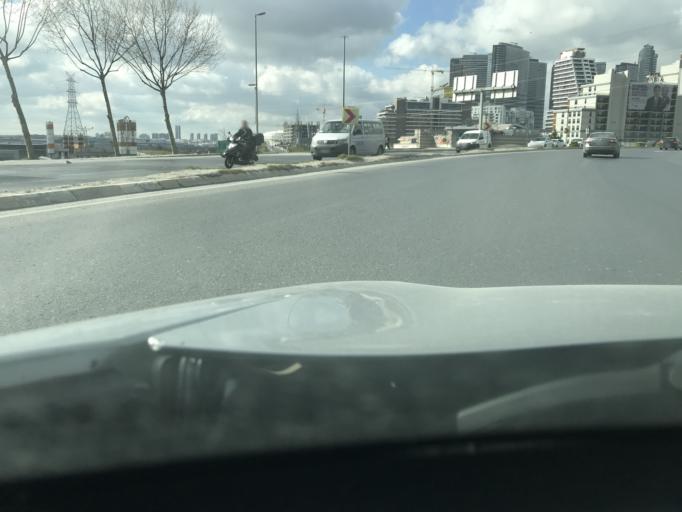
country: TR
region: Istanbul
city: Esenyurt
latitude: 41.0526
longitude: 28.6706
